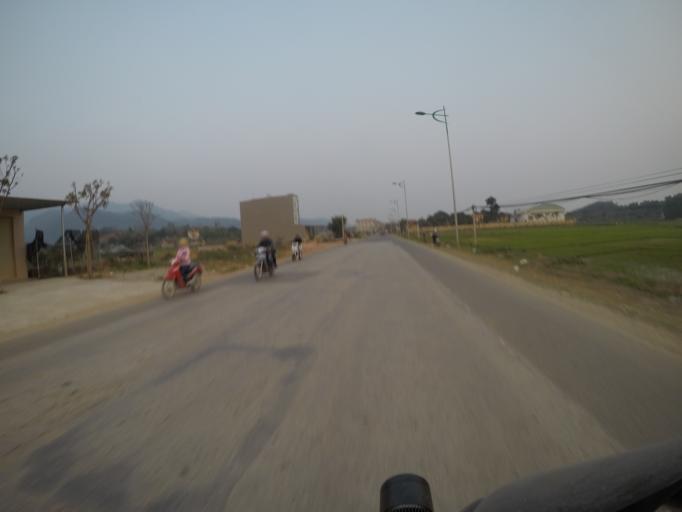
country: VN
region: Vinh Phuc
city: Trai Ngau
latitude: 21.4285
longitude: 105.5892
